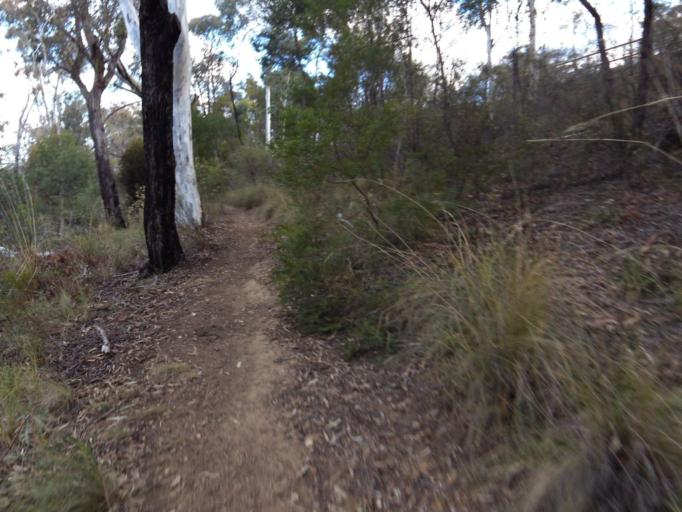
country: AU
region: Australian Capital Territory
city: Acton
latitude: -35.2641
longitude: 149.1112
